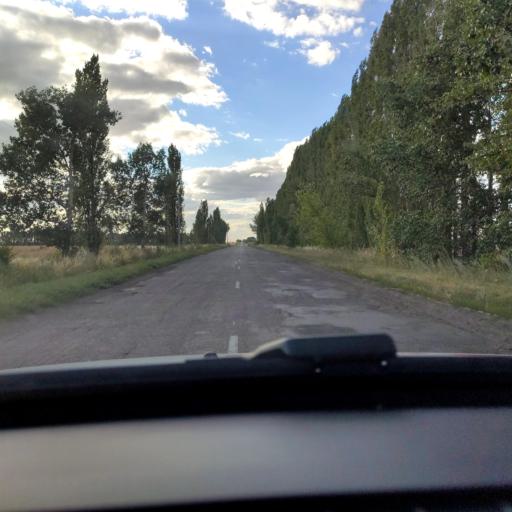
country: RU
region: Voronezj
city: Orlovo
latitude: 51.6164
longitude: 39.7930
